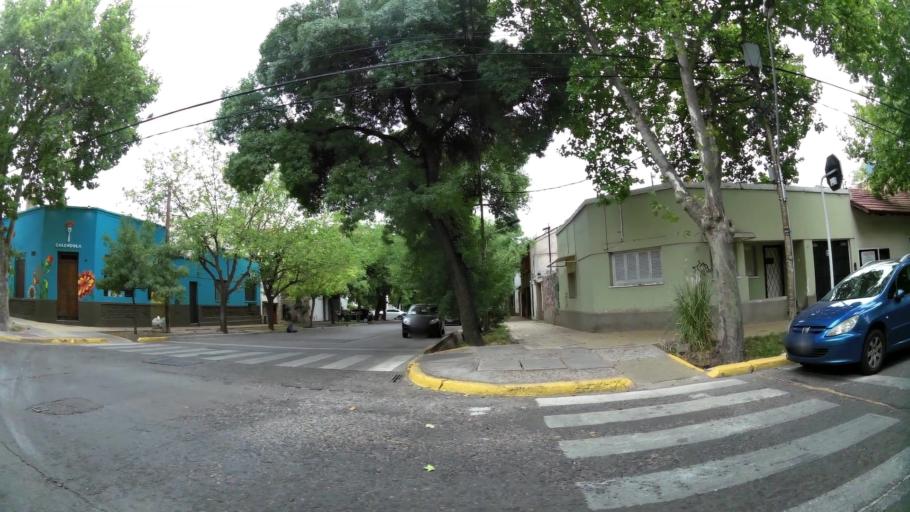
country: AR
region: Mendoza
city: Mendoza
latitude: -32.8886
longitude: -68.8512
